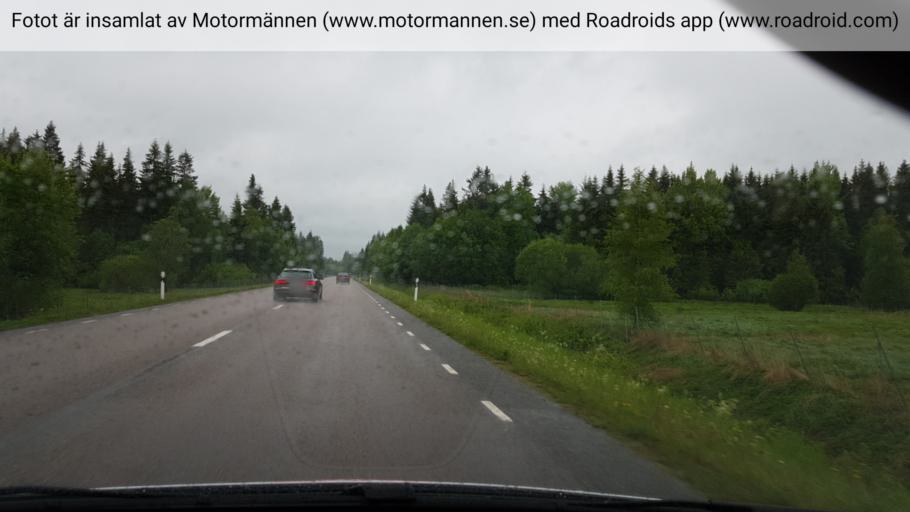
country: SE
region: Vaestra Goetaland
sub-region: Falkopings Kommun
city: Falkoeping
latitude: 58.0515
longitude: 13.5453
